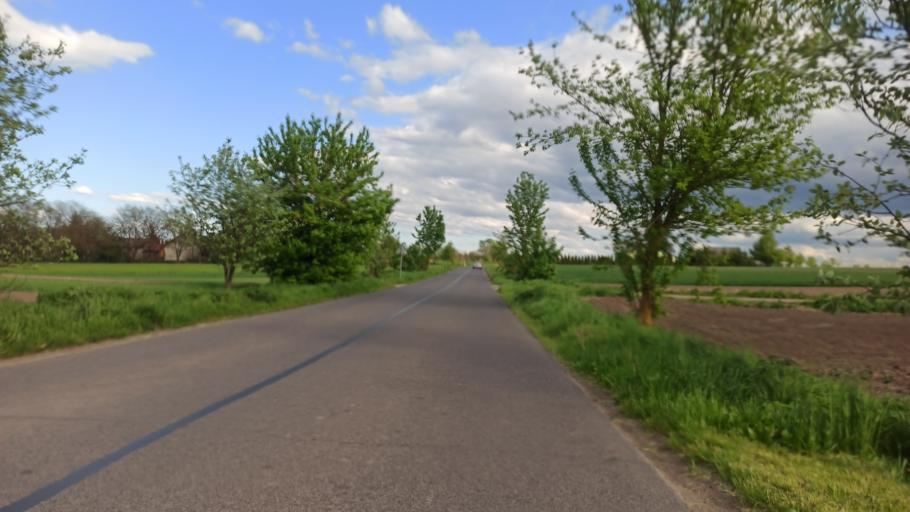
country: PL
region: Subcarpathian Voivodeship
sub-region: Powiat jaroslawski
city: Sosnica
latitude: 49.9218
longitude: 22.8537
